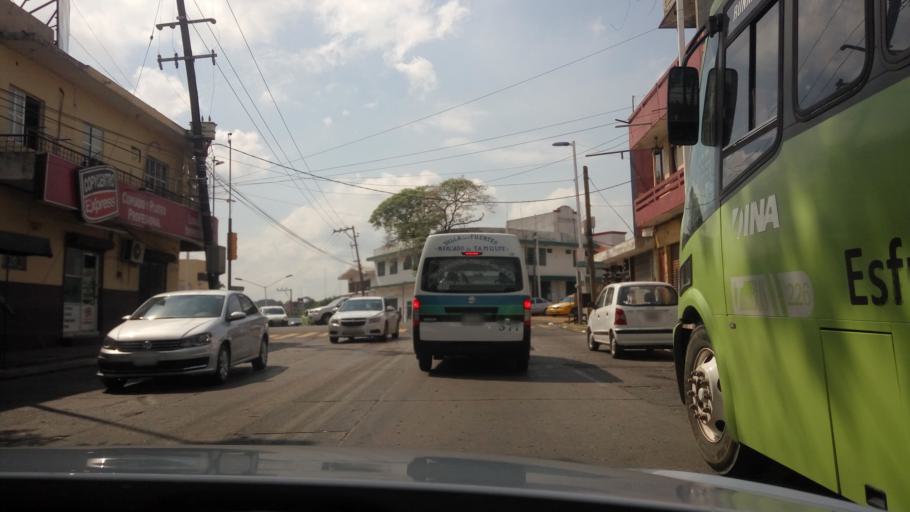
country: MX
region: Tabasco
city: Villahermosa
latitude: 17.9902
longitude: -92.9248
